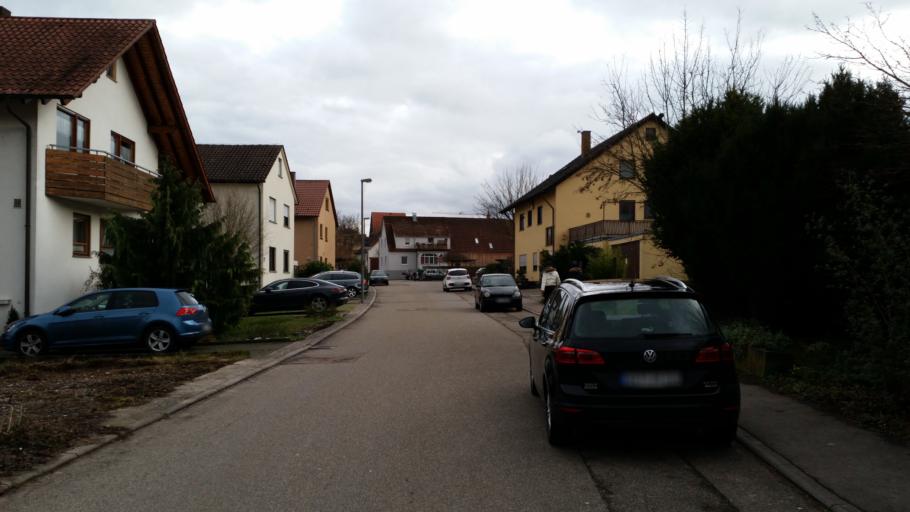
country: DE
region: Baden-Wuerttemberg
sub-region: Regierungsbezirk Stuttgart
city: Besigheim
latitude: 49.0037
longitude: 9.1405
